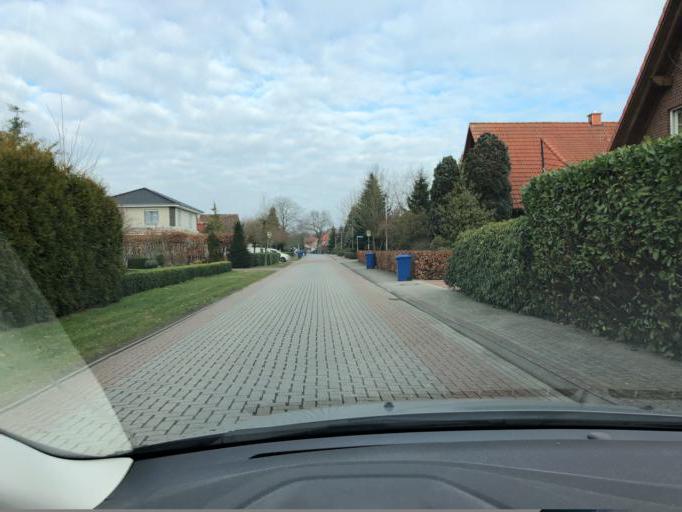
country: DE
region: Lower Saxony
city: Bad Zwischenahn
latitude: 53.1780
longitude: 8.0460
